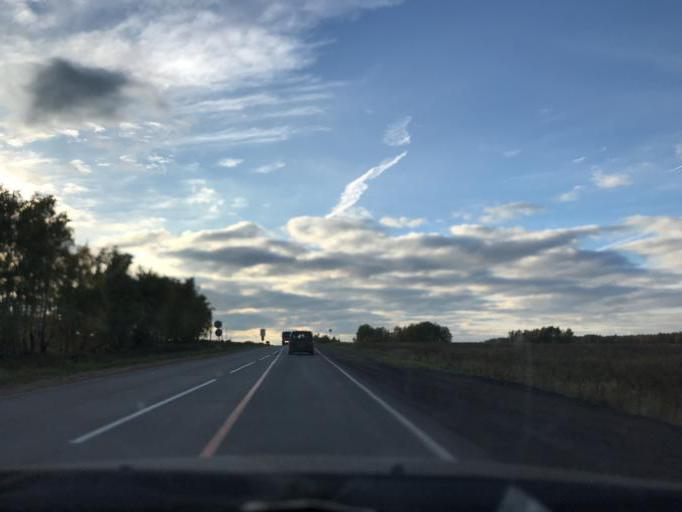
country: RU
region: Kaluga
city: Kurovskoye
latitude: 54.5290
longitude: 35.9707
